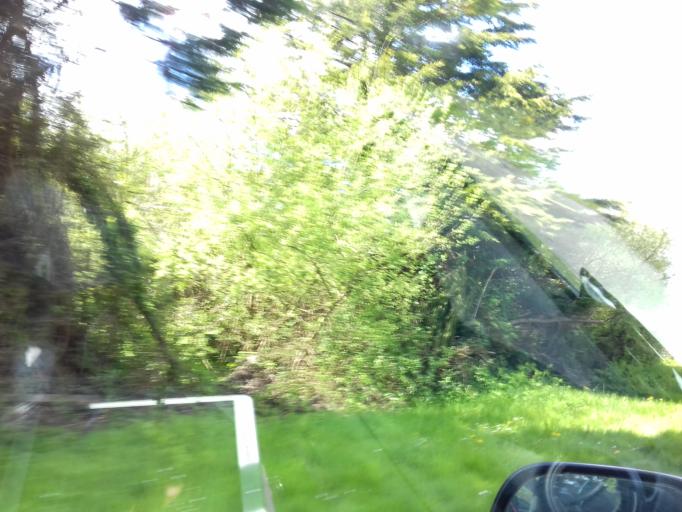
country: IE
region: Leinster
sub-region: Loch Garman
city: Castlebridge
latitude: 52.3692
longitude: -6.4475
